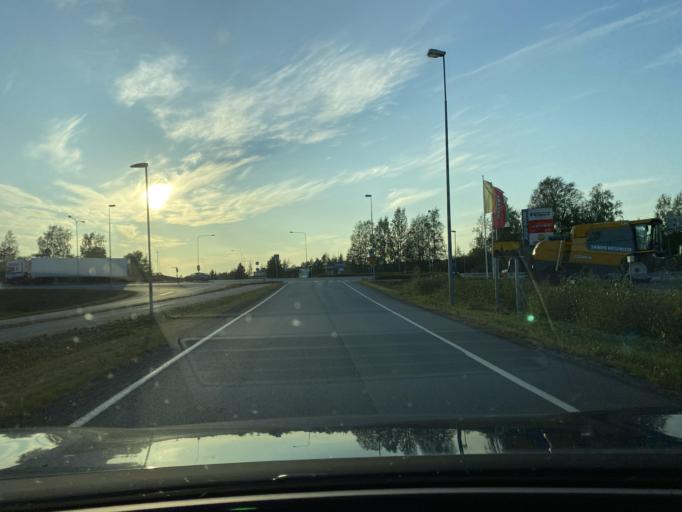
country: FI
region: Southern Ostrobothnia
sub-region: Seinaejoki
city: Nurmo
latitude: 62.8086
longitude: 22.8802
